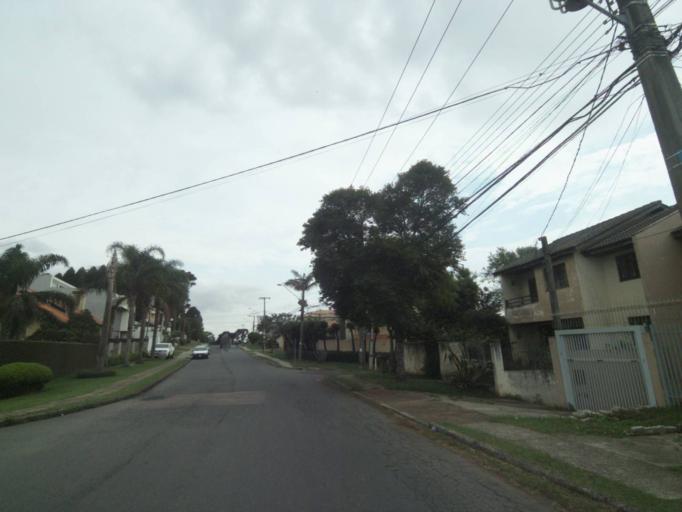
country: BR
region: Parana
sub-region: Curitiba
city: Curitiba
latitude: -25.3943
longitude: -49.2956
